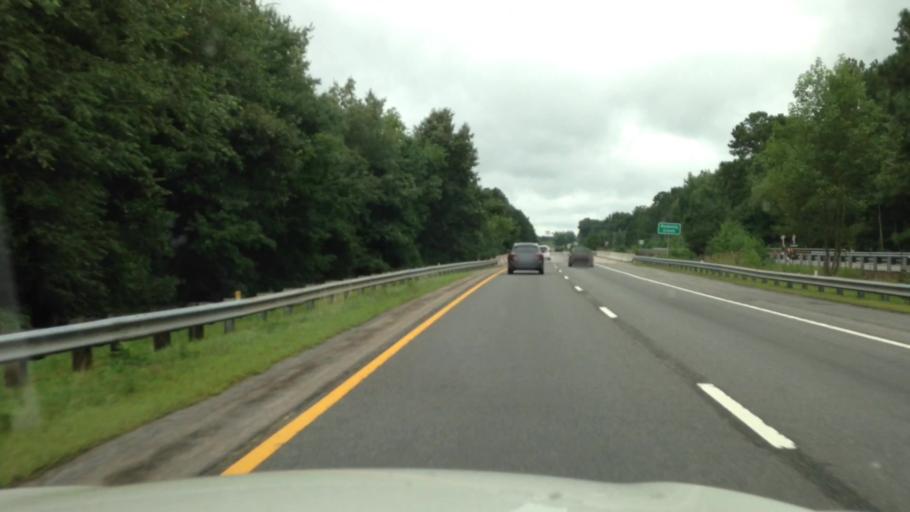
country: US
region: Virginia
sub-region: Sussex County
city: Sussex
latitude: 36.9936
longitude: -77.3925
